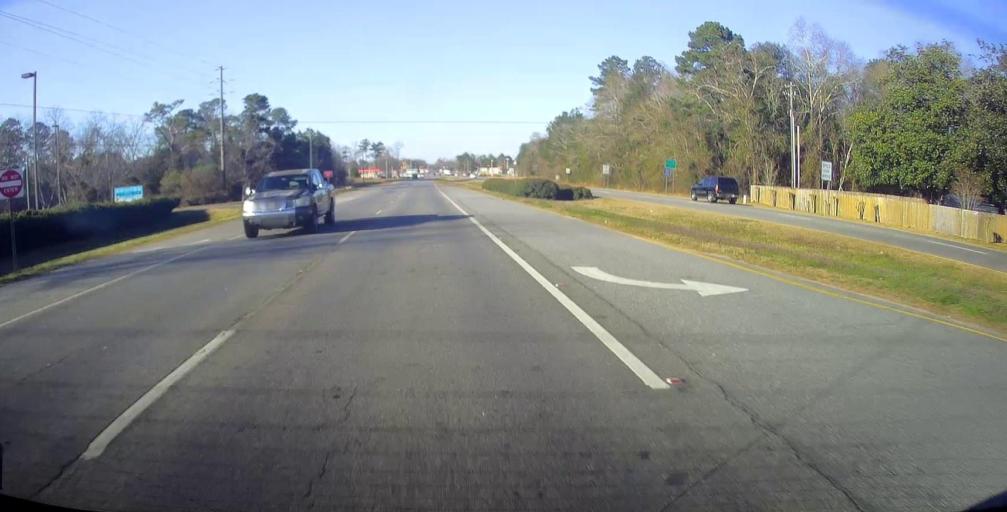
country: US
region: Georgia
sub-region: Lee County
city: Leesburg
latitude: 31.7154
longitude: -84.1725
